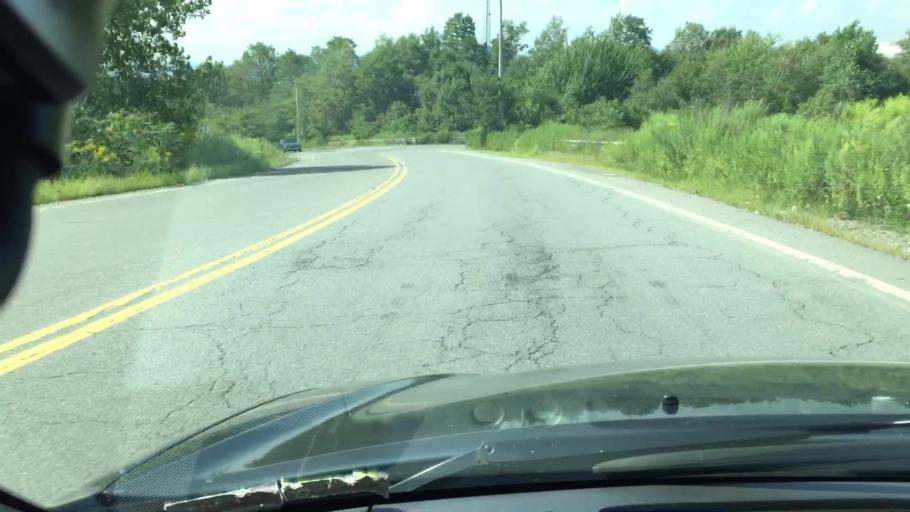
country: US
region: Pennsylvania
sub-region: Luzerne County
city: Ashley
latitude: 41.2012
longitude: -75.9193
